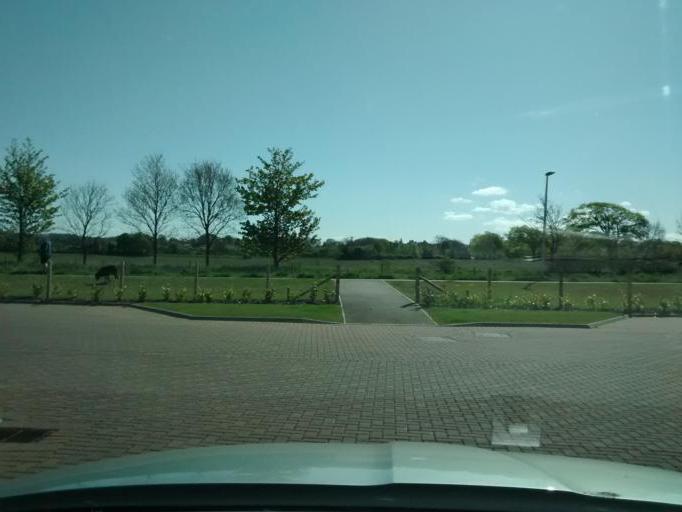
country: GB
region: Scotland
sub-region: West Lothian
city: Broxburn
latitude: 55.9612
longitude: -3.4719
